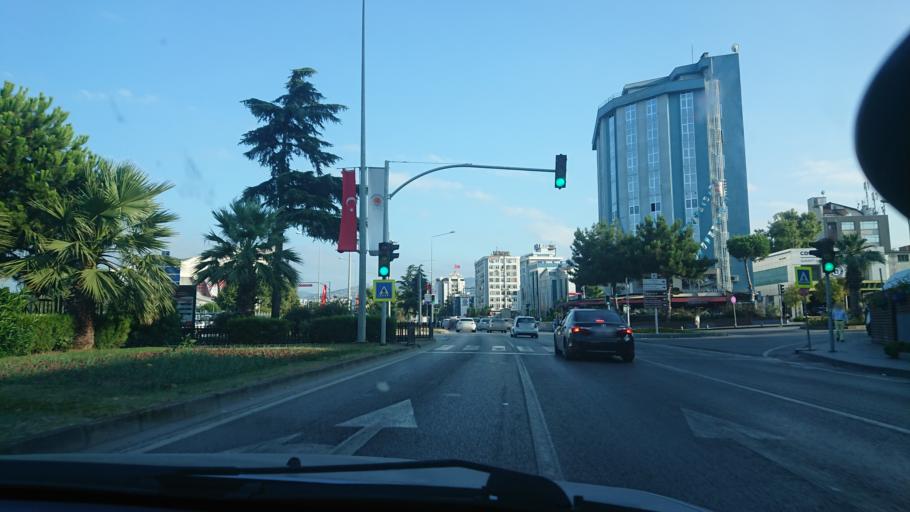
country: TR
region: Samsun
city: Samsun
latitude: 41.2964
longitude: 36.3329
